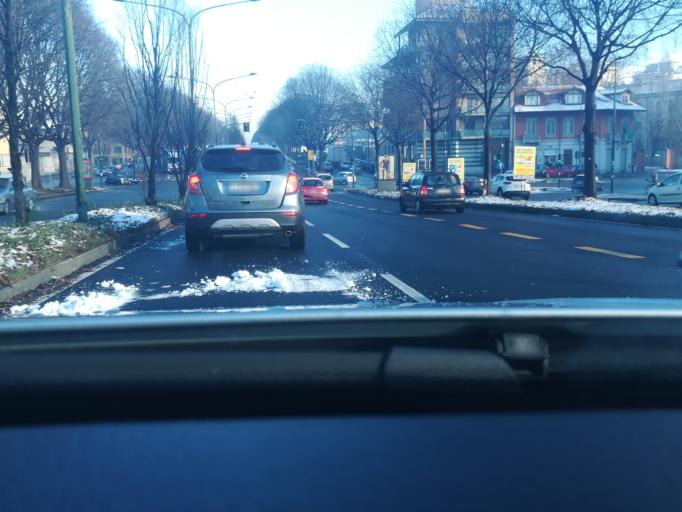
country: IT
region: Piedmont
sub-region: Provincia di Torino
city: Turin
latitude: 45.0911
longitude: 7.6541
